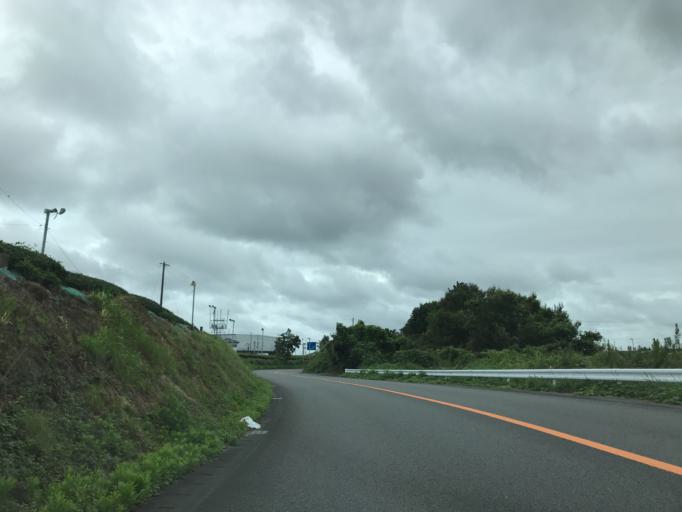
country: JP
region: Shizuoka
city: Kanaya
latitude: 34.7735
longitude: 138.1404
